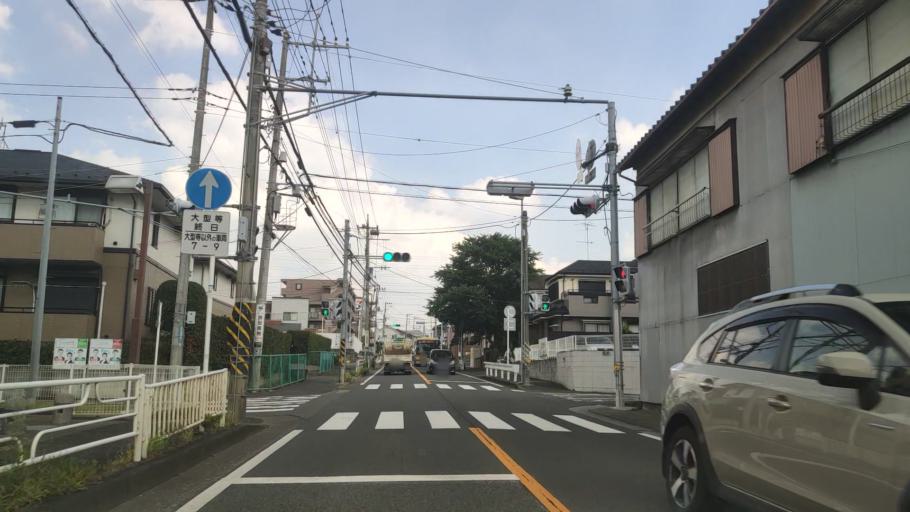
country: JP
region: Kanagawa
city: Minami-rinkan
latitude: 35.4498
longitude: 139.5034
